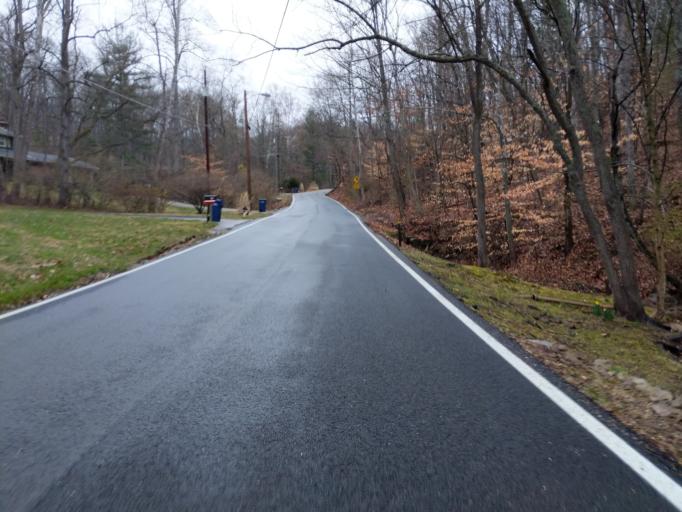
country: US
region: Ohio
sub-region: Athens County
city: Athens
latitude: 39.3421
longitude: -82.0885
